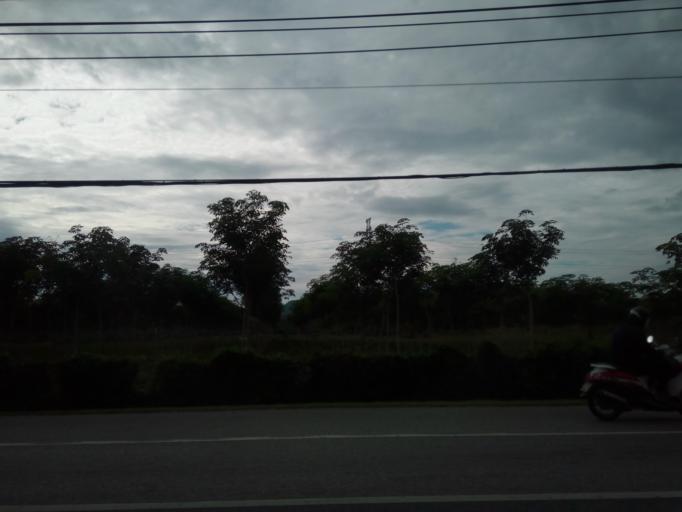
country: TH
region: Phuket
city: Thalang
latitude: 8.0385
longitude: 98.3340
